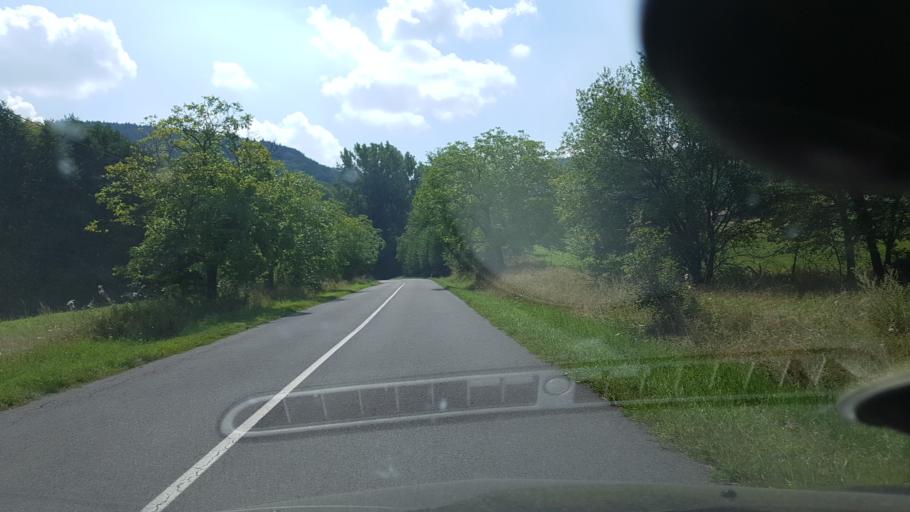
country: SK
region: Banskobystricky
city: Detva
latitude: 48.4986
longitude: 19.3230
